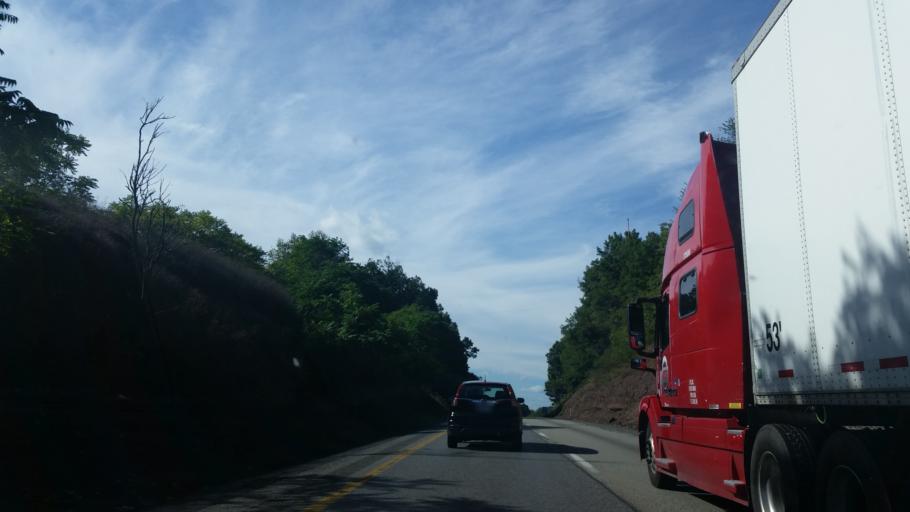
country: US
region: Pennsylvania
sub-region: Bedford County
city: Earlston
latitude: 39.9971
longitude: -78.2397
